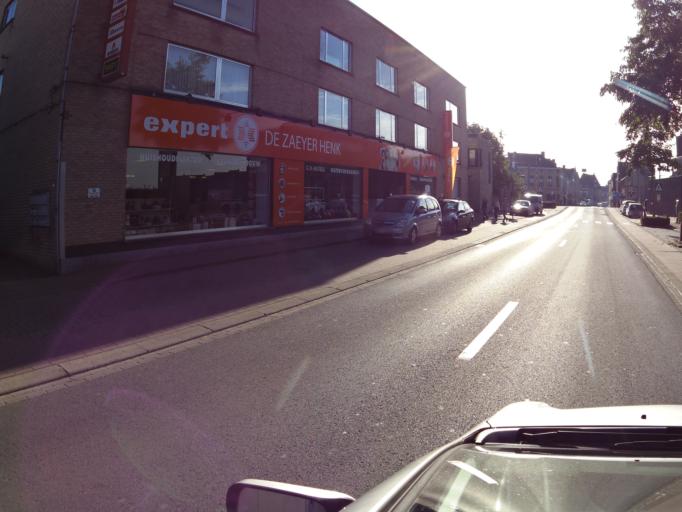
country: BE
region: Flanders
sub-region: Provincie West-Vlaanderen
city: Veurne
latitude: 51.0746
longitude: 2.6700
